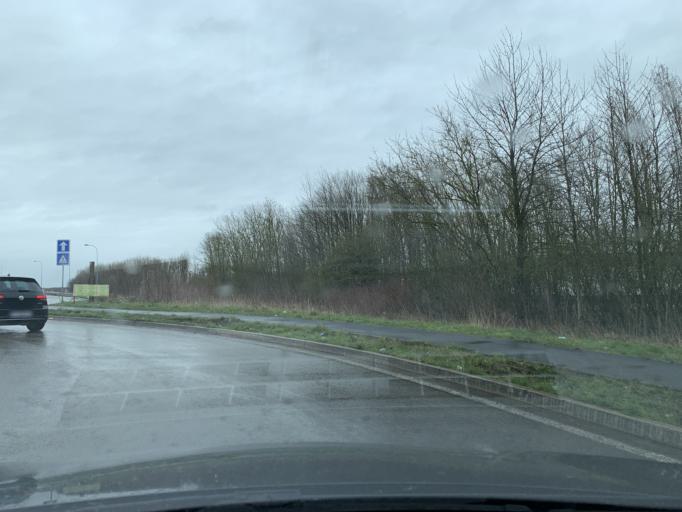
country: FR
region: Nord-Pas-de-Calais
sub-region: Departement du Nord
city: La Sentinelle
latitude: 50.3383
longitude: 3.4704
